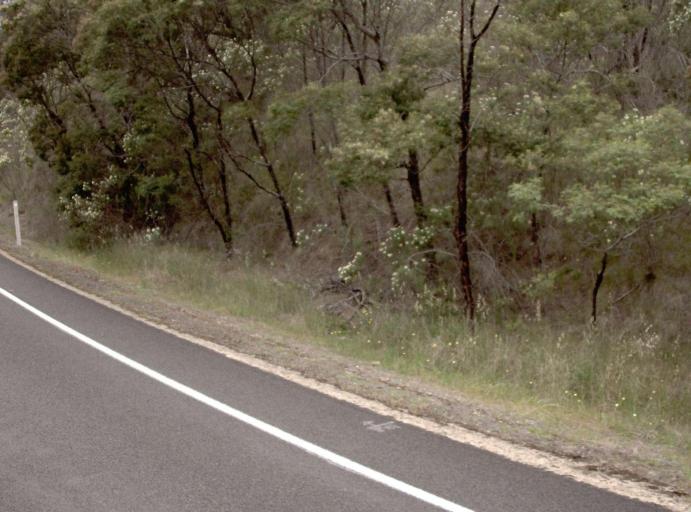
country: AU
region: New South Wales
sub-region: Bombala
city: Bombala
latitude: -37.2509
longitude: 149.2503
